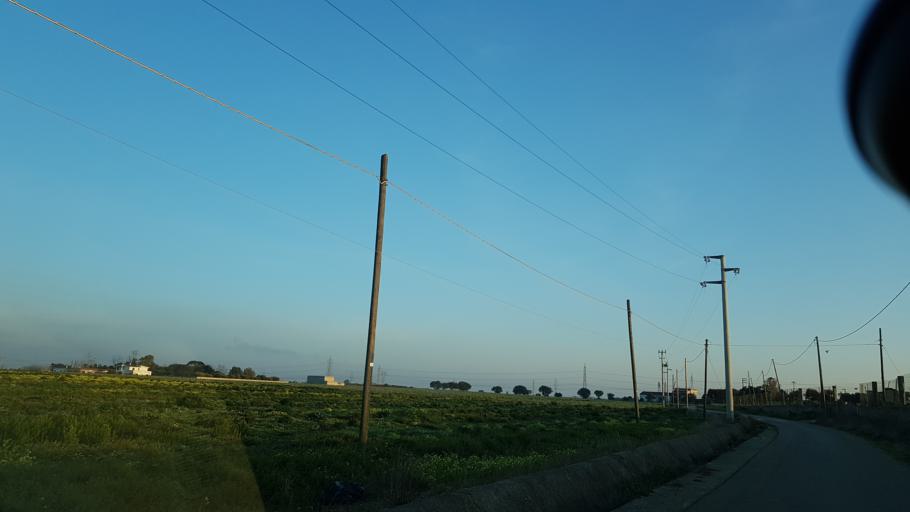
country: IT
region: Apulia
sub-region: Provincia di Brindisi
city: La Rosa
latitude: 40.6068
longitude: 17.9383
